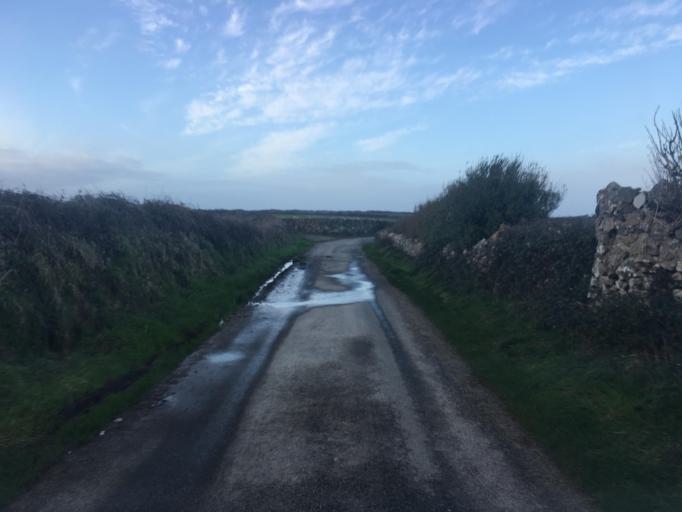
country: FR
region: Lower Normandy
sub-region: Departement de la Manche
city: Beaumont-Hague
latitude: 49.7219
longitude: -1.9222
